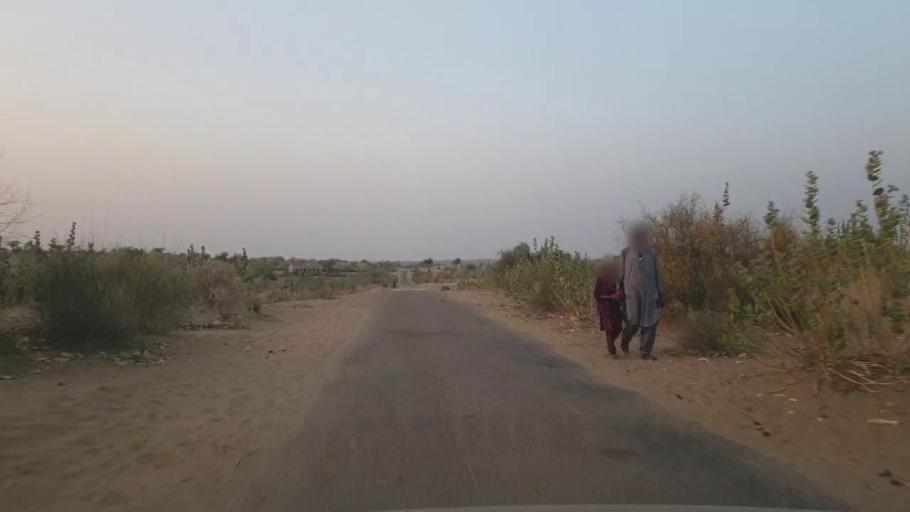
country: PK
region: Sindh
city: Umarkot
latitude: 25.2892
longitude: 70.0780
